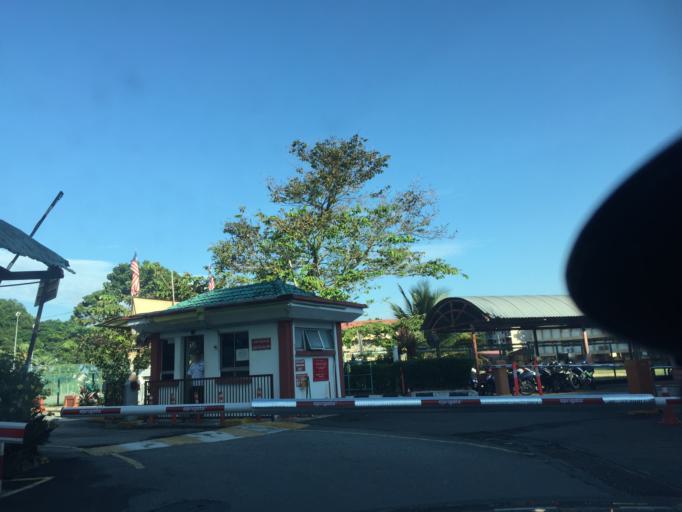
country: MY
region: Kuala Lumpur
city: Kuala Lumpur
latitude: 3.2072
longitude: 101.7351
